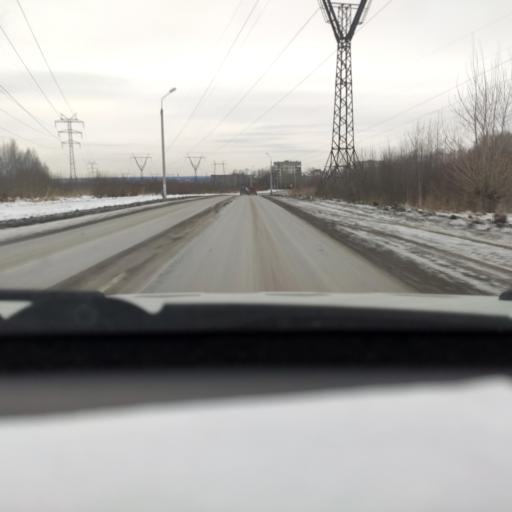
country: RU
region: Perm
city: Perm
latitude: 58.0987
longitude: 56.3938
